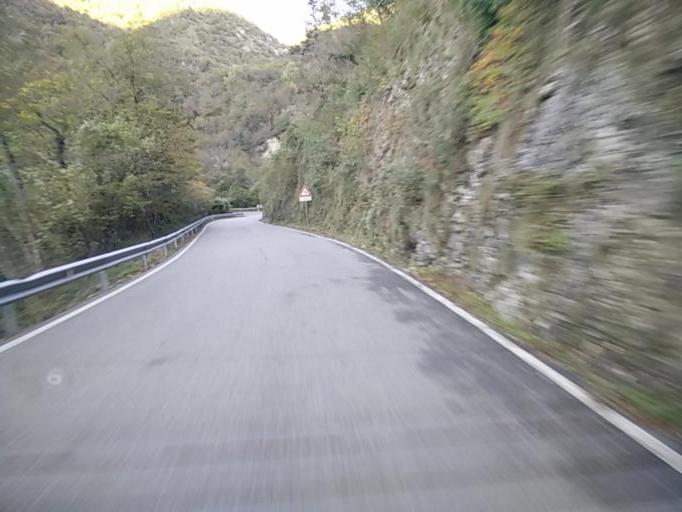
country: IT
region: Lombardy
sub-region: Provincia di Brescia
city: Gargnano
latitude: 45.6860
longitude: 10.6142
